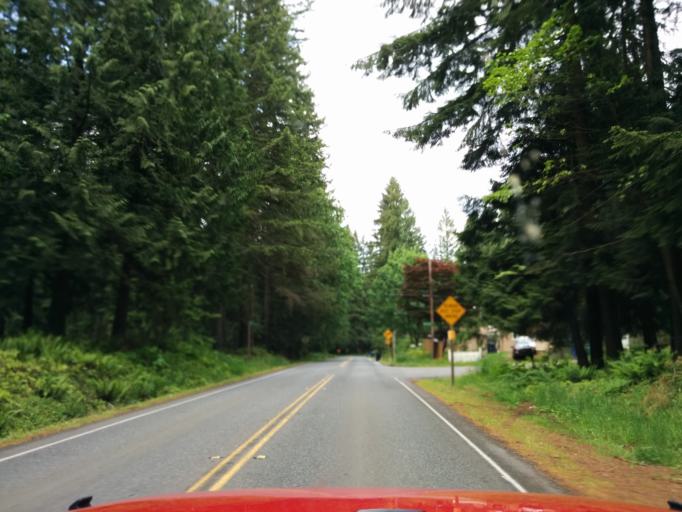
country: US
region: Washington
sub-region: King County
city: Ames Lake
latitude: 47.6391
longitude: -121.9685
